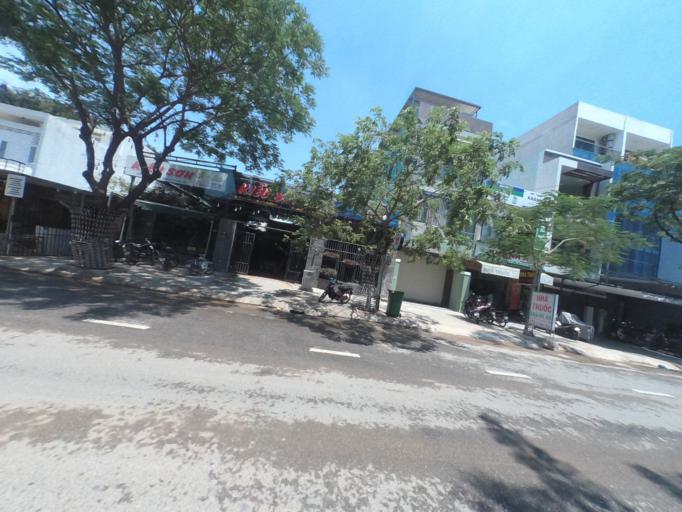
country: VN
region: Da Nang
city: Lien Chieu
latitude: 16.0704
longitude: 108.1724
